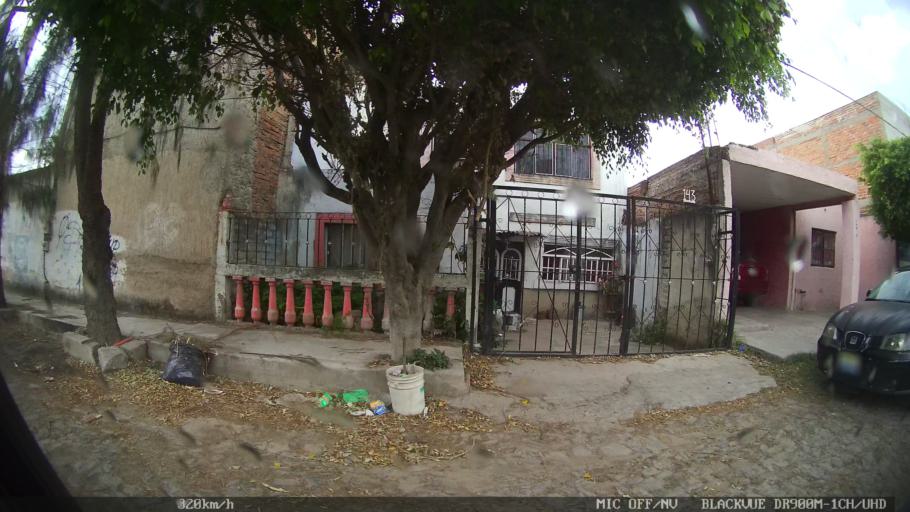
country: MX
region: Jalisco
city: Tonala
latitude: 20.6204
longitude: -103.2634
